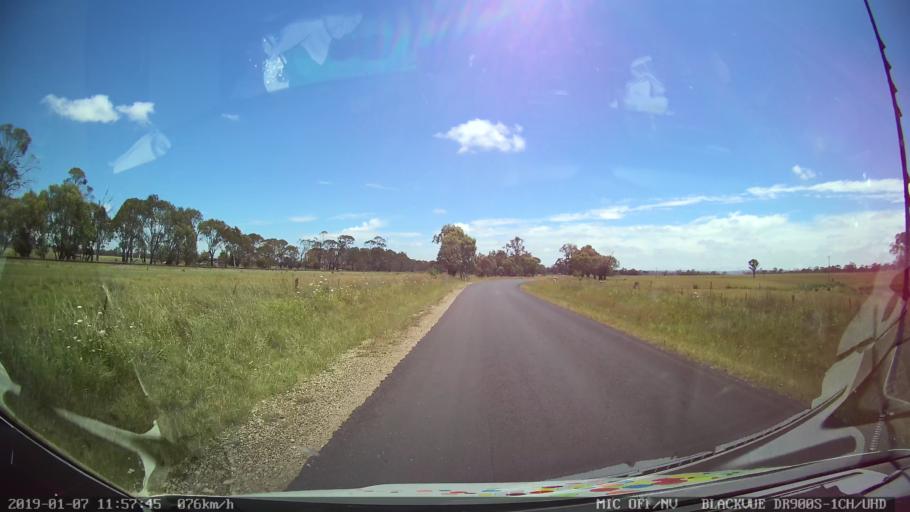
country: AU
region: New South Wales
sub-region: Guyra
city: Guyra
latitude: -30.2609
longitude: 151.6660
